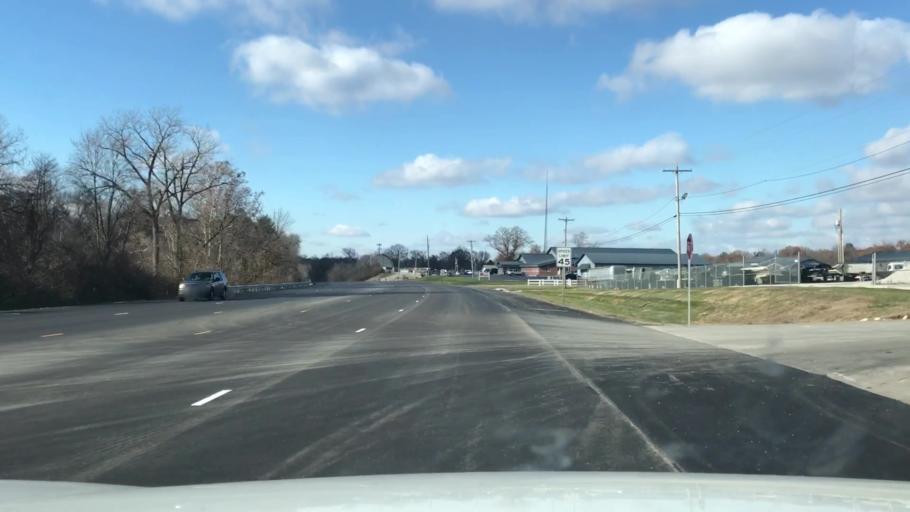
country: US
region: Illinois
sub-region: Saint Clair County
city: Swansea
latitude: 38.5592
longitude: -90.0219
